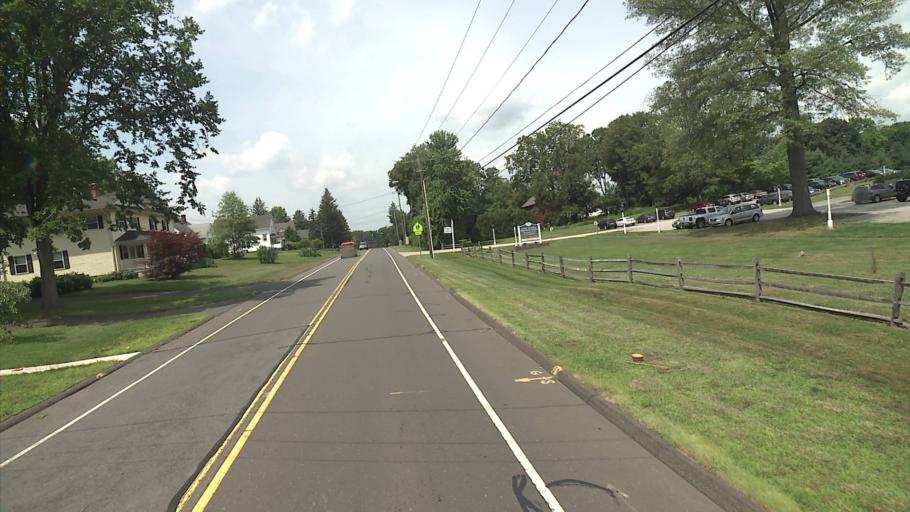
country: US
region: Connecticut
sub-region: Middlesex County
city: Middletown
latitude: 41.5328
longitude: -72.6401
